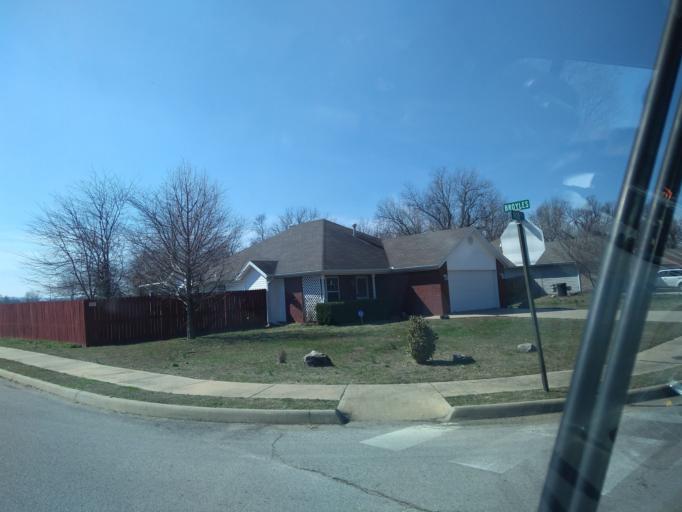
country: US
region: Arkansas
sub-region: Washington County
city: Farmington
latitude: 36.0492
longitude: -94.2360
